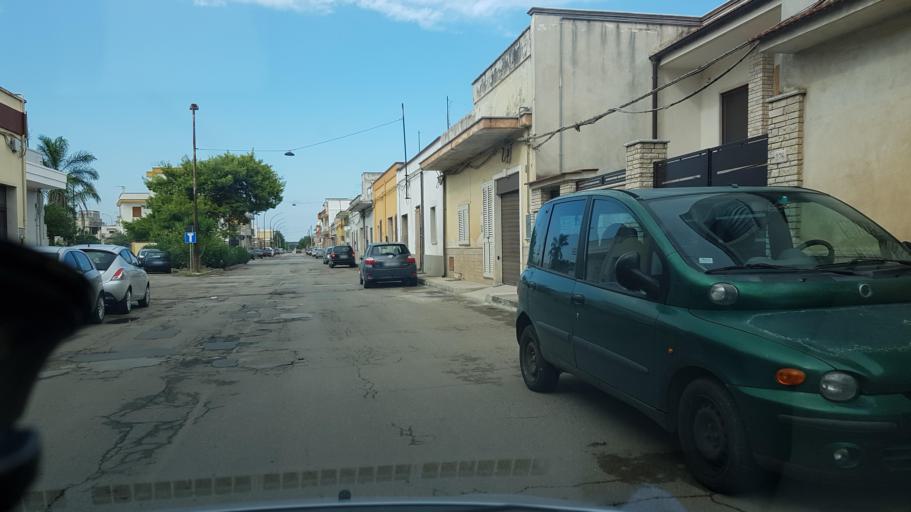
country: IT
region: Apulia
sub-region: Provincia di Brindisi
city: Torre Santa Susanna
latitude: 40.4722
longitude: 17.7398
